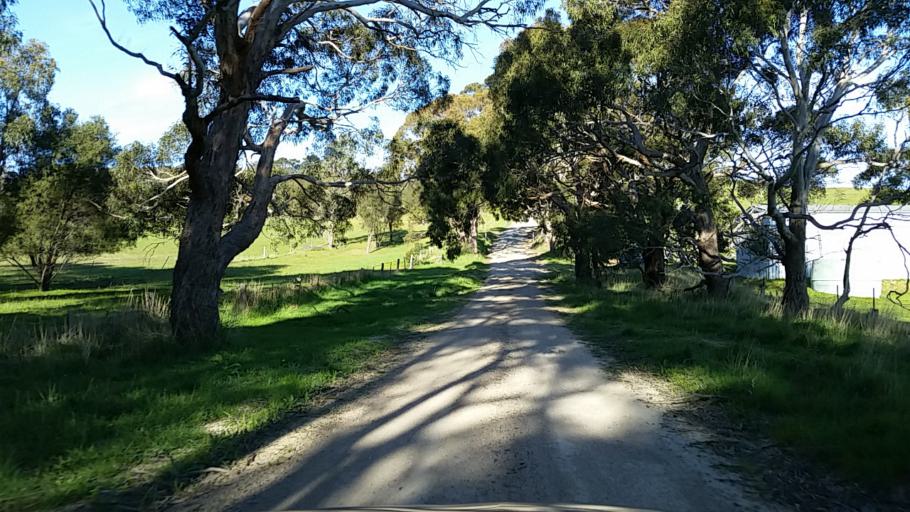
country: AU
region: South Australia
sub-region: Mount Barker
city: Meadows
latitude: -35.1913
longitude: 138.7778
